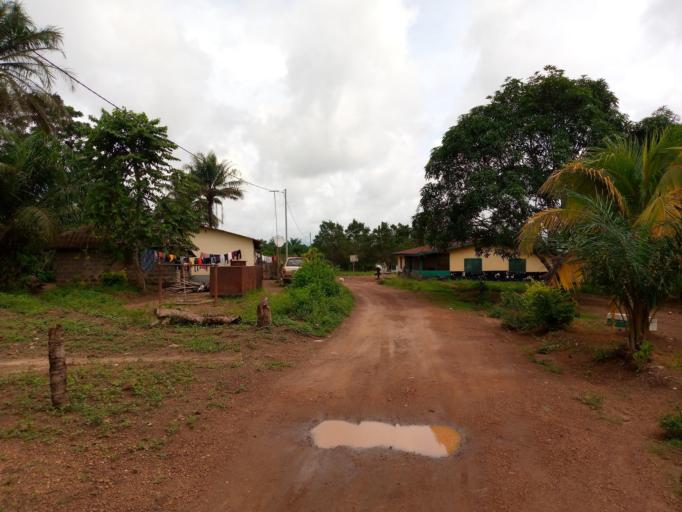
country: SL
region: Southern Province
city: Mogbwemo
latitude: 7.7651
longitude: -12.3112
